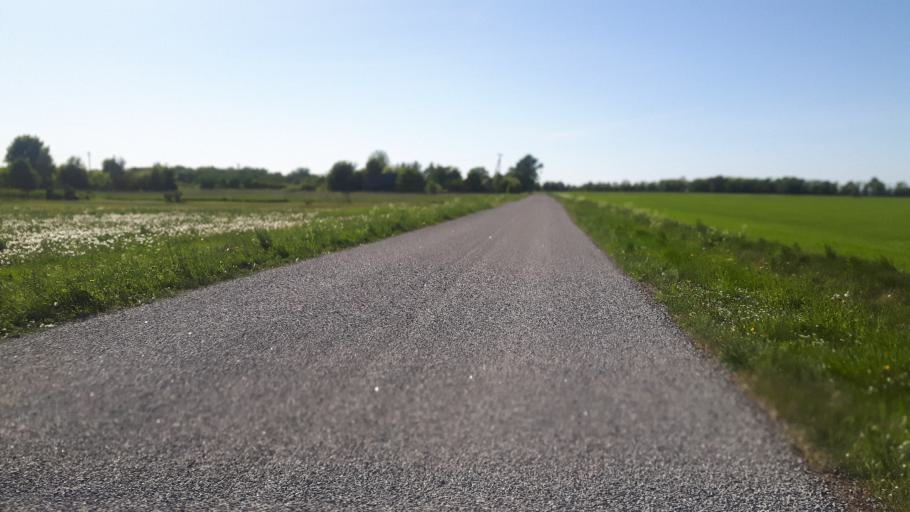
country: EE
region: Ida-Virumaa
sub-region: Kohtla-Jaerve linn
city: Kohtla-Jarve
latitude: 59.4358
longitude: 27.2017
